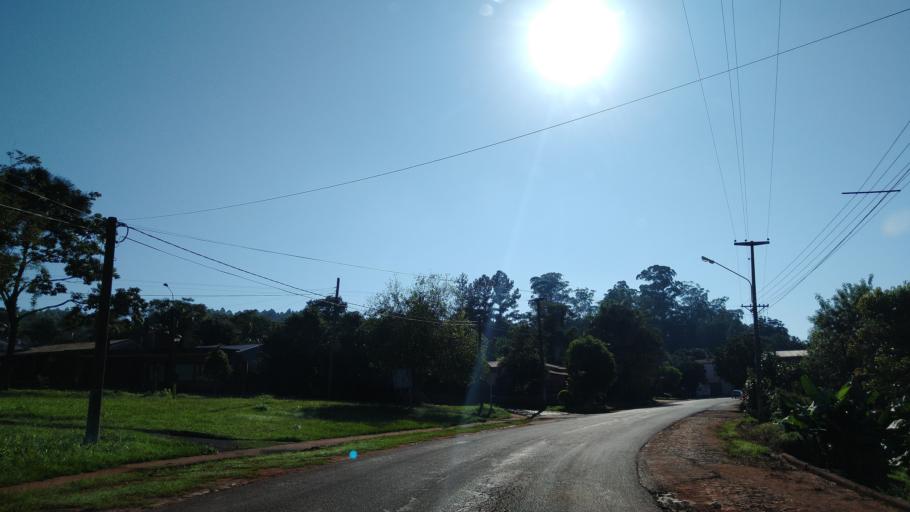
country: AR
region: Misiones
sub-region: Departamento de Montecarlo
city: Montecarlo
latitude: -26.5610
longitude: -54.7808
